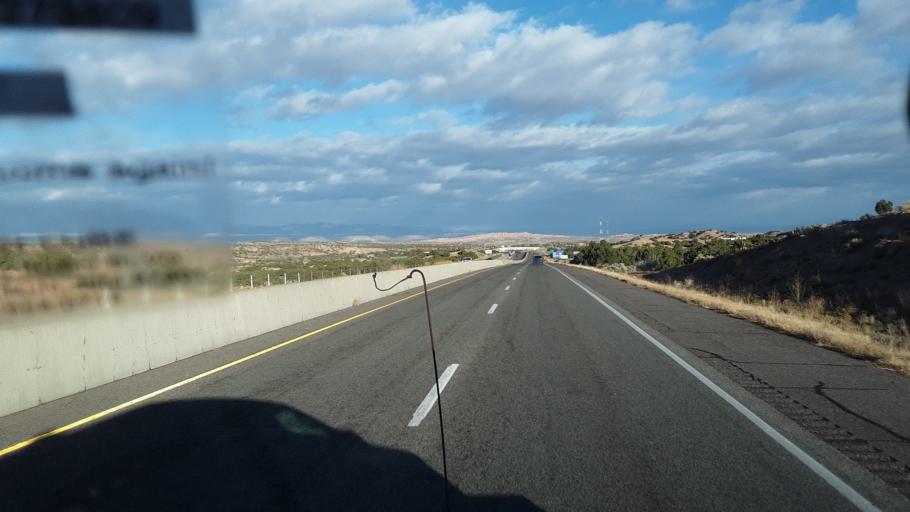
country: US
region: New Mexico
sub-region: Santa Fe County
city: Nambe
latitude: 35.8343
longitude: -105.9825
